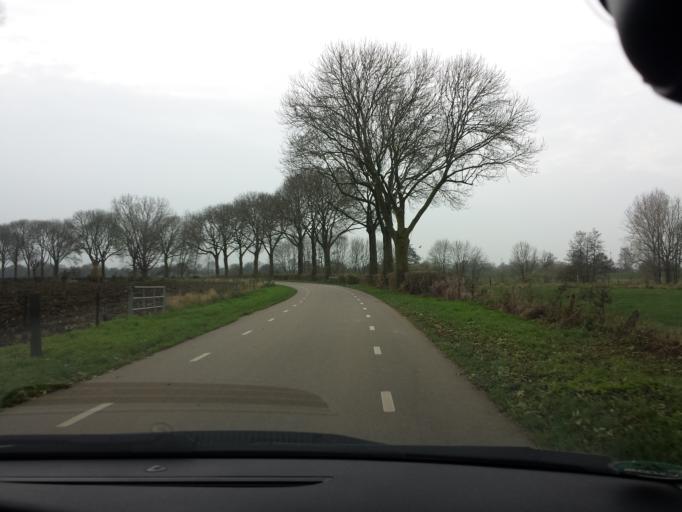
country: NL
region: North Brabant
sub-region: Gemeente Cuijk
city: Cuijk
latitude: 51.7440
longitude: 5.8843
